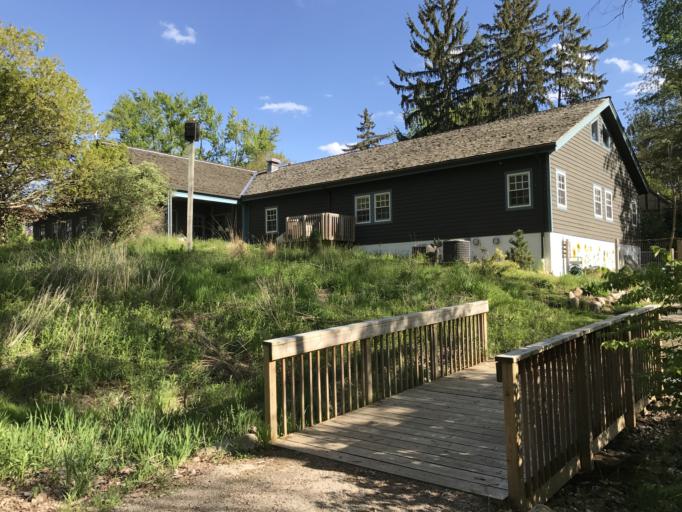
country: US
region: Michigan
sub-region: Oakland County
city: Farmington Hills
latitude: 42.4767
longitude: -83.3793
